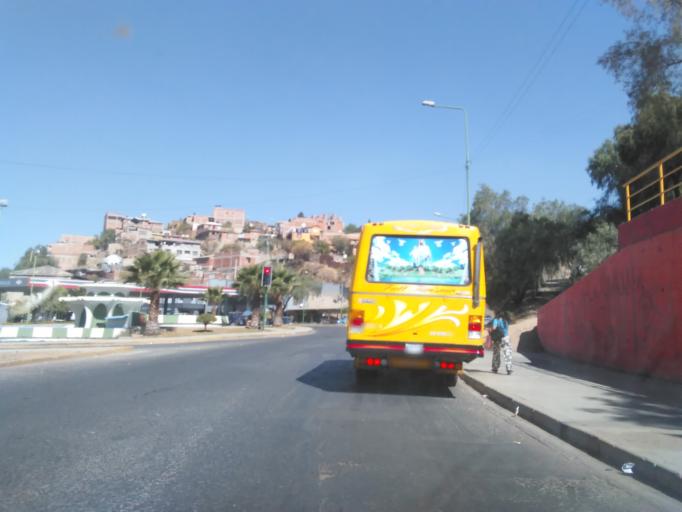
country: BO
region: Cochabamba
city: Cochabamba
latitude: -17.4059
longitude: -66.1454
